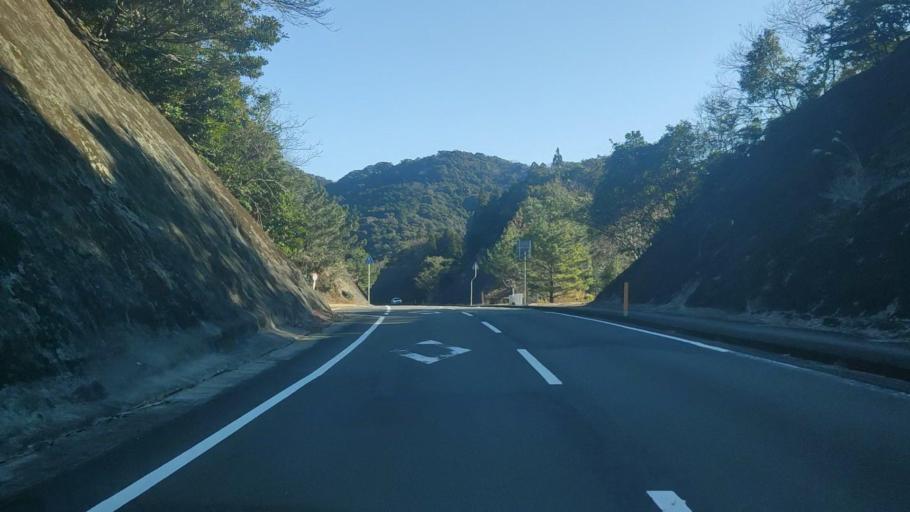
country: JP
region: Miyazaki
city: Nobeoka
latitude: 32.6617
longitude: 131.7637
